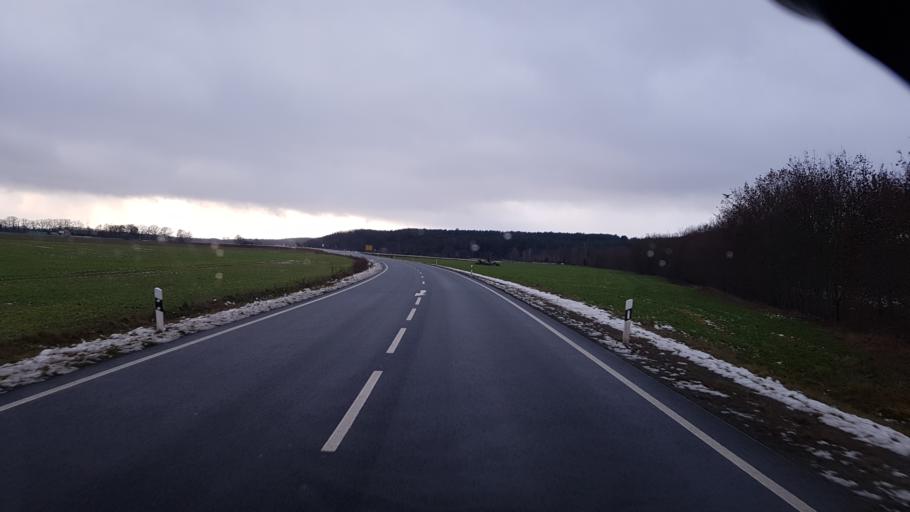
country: DE
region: Brandenburg
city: Schenkendobern
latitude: 51.8789
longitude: 14.6332
